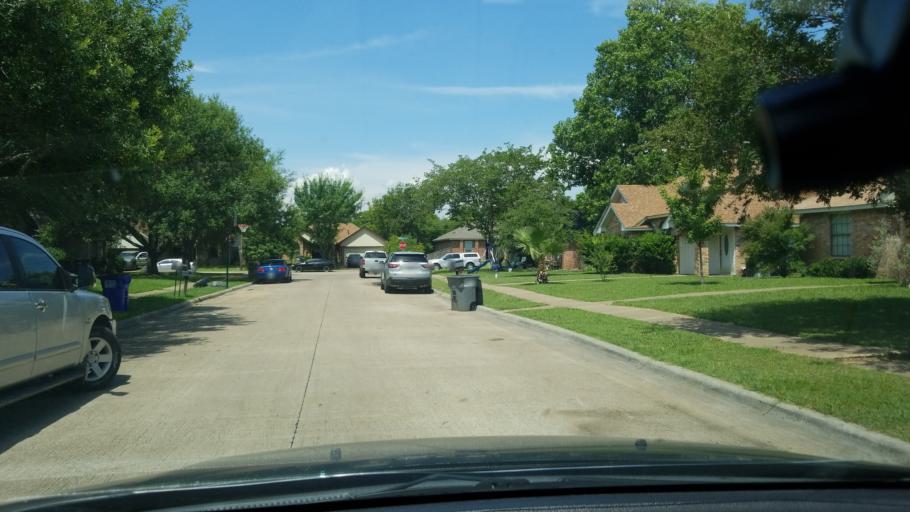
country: US
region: Texas
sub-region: Dallas County
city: Balch Springs
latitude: 32.7405
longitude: -96.6246
